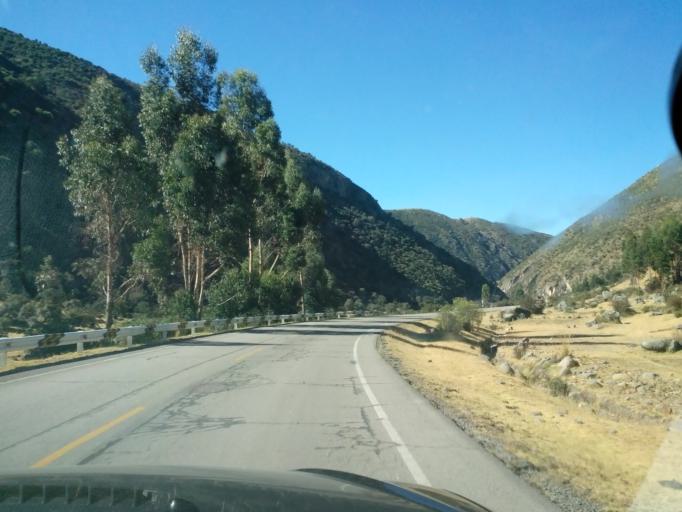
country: PE
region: Ayacucho
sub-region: Provincia de Huamanga
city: Vinchos
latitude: -13.3451
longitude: -74.3946
